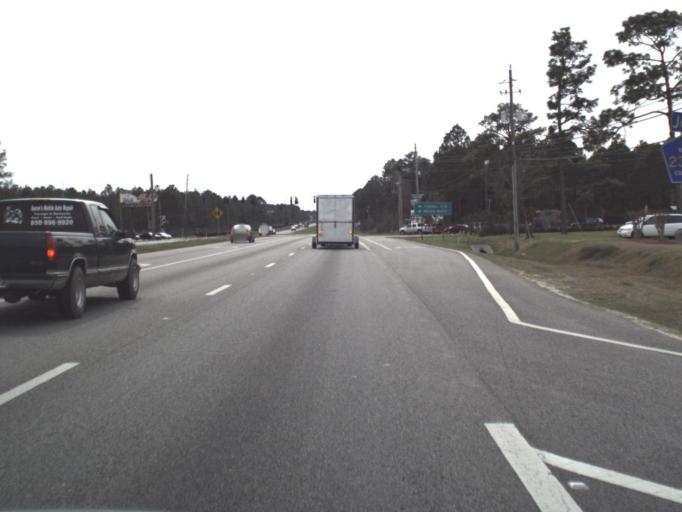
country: US
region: Florida
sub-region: Bay County
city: Hiland Park
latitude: 30.2142
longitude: -85.6062
